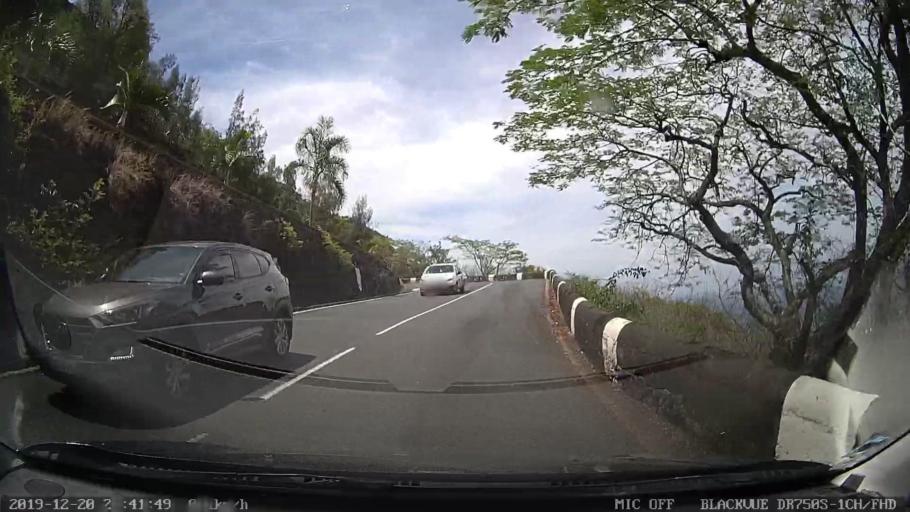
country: RE
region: Reunion
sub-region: Reunion
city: Saint-Denis
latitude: -20.8852
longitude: 55.4381
